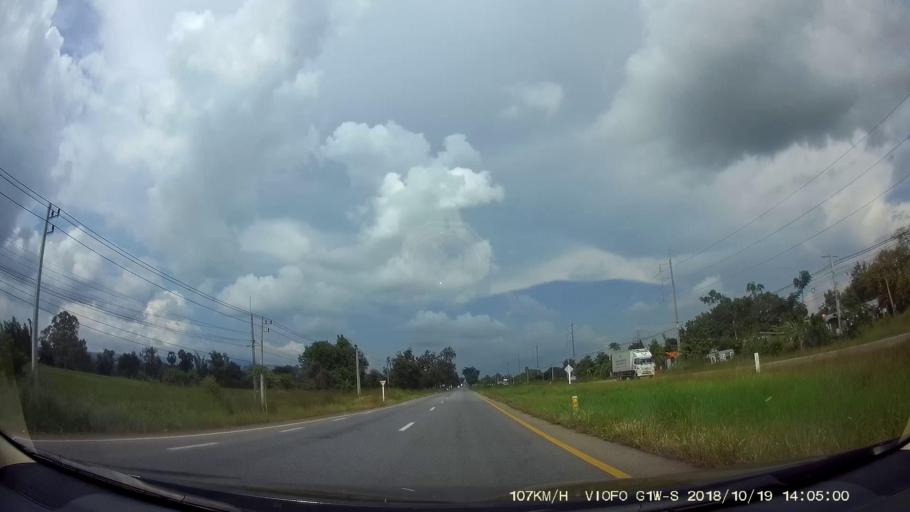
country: TH
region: Chaiyaphum
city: Chaiyaphum
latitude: 15.8701
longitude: 102.0879
